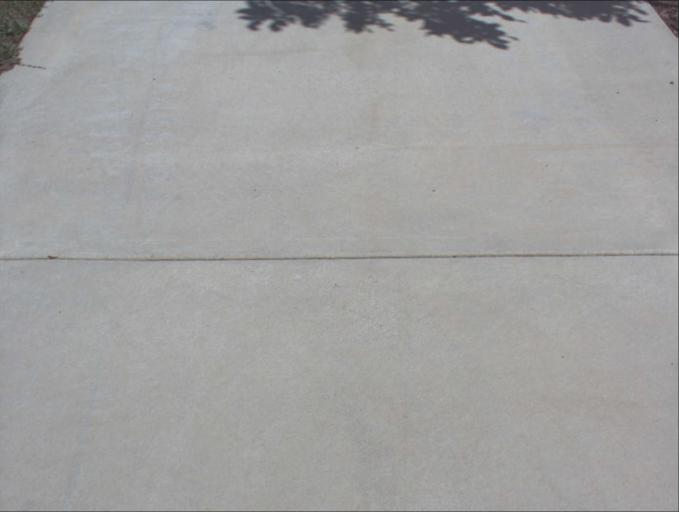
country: AU
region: Queensland
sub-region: Logan
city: Chambers Flat
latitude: -27.8059
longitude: 153.1066
